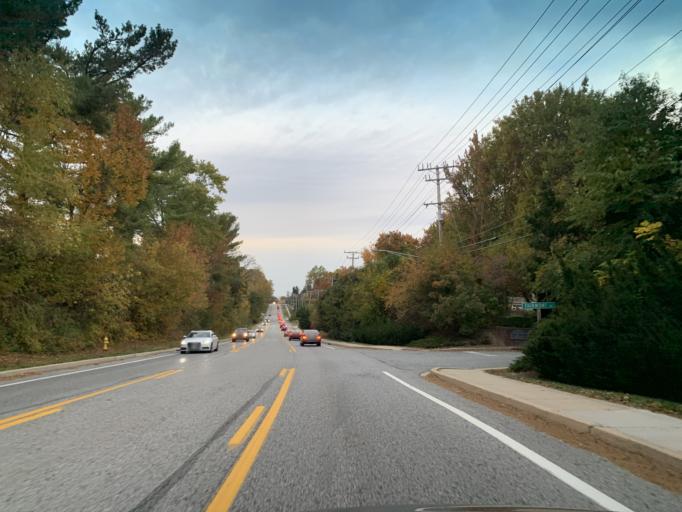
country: US
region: Maryland
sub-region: Harford County
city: South Bel Air
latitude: 39.5208
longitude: -76.3357
